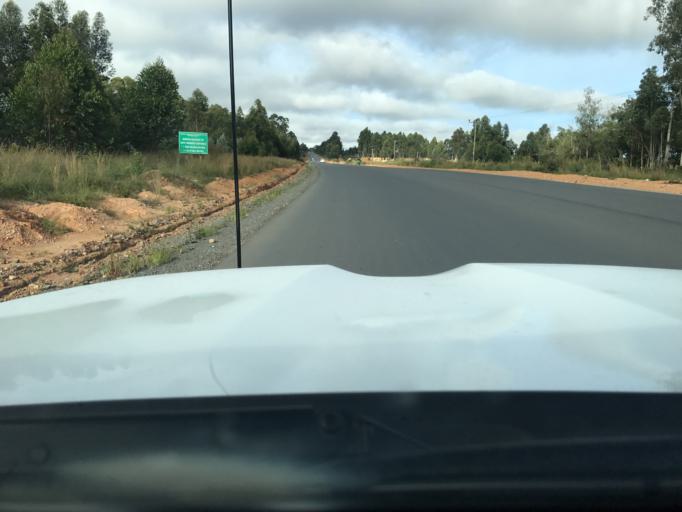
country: TZ
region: Iringa
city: Makungu
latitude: -8.3088
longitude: 35.2856
